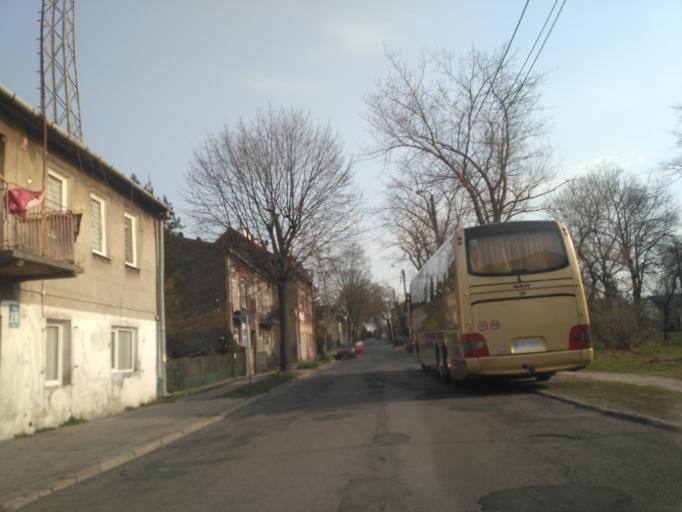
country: PL
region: Lublin Voivodeship
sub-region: Powiat lubelski
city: Lublin
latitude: 51.2310
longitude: 22.5792
